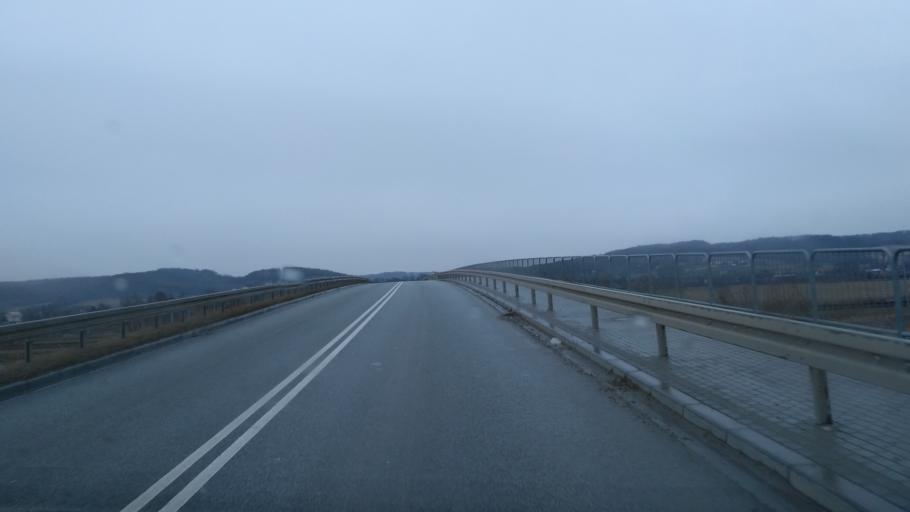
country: PL
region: Subcarpathian Voivodeship
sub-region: Powiat debicki
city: Brzeznica
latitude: 50.0669
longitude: 21.4738
